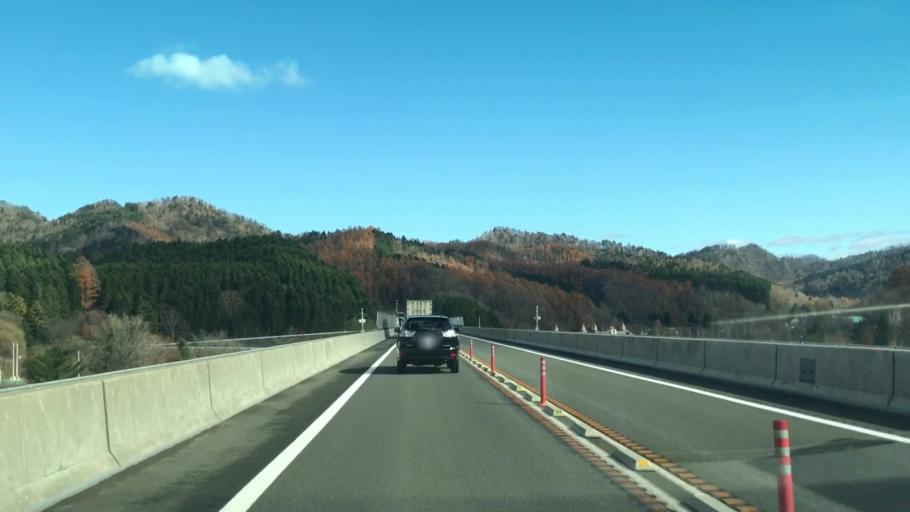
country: JP
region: Hokkaido
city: Iwamizawa
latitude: 42.9336
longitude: 142.0798
